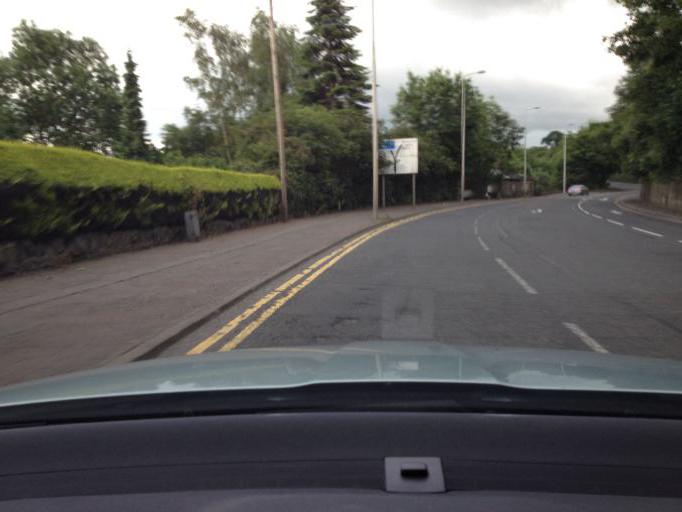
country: GB
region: Scotland
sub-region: Perth and Kinross
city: Perth
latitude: 56.3766
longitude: -3.4301
